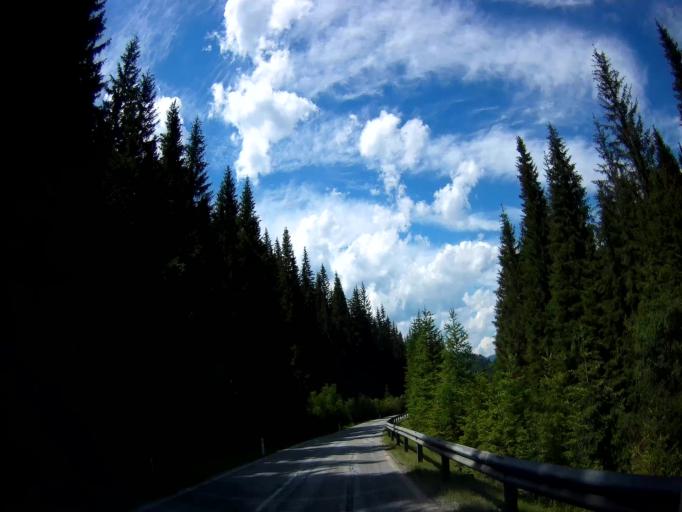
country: AT
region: Styria
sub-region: Politischer Bezirk Murau
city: Stadl an der Mur
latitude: 47.0024
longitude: 14.0120
